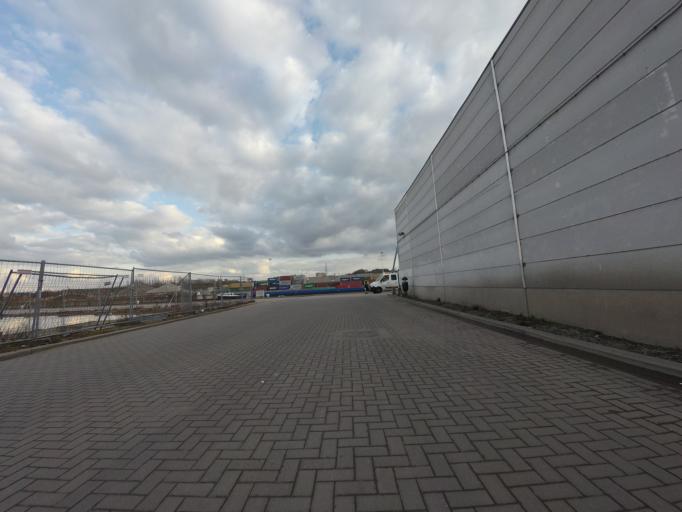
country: BE
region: Flanders
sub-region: Provincie Vlaams-Brabant
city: Grimbergen
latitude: 50.8864
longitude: 4.3830
